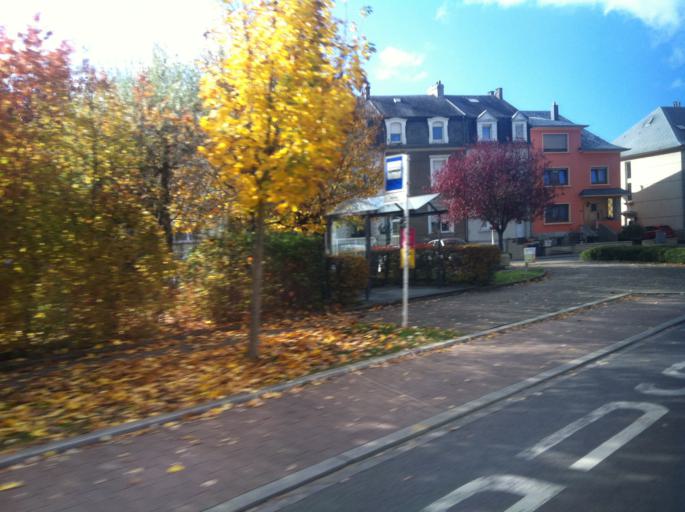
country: FR
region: Lorraine
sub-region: Departement de la Moselle
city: Russange
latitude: 49.4948
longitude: 5.9552
